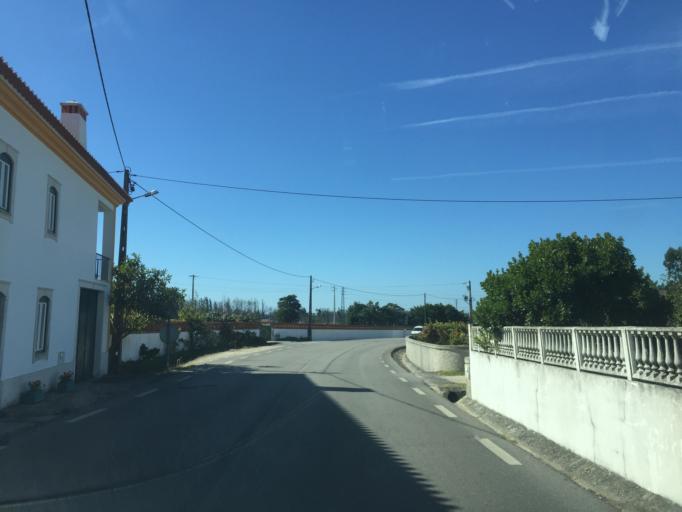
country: PT
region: Coimbra
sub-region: Montemor-O-Velho
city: Arazede
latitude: 40.3156
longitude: -8.7571
